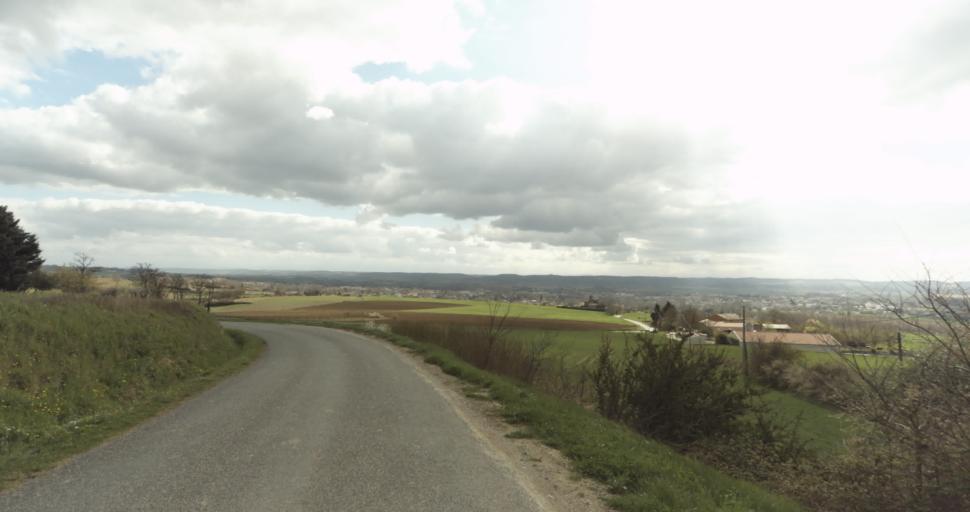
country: FR
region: Midi-Pyrenees
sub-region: Departement de la Haute-Garonne
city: Auterive
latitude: 43.3663
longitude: 1.4844
